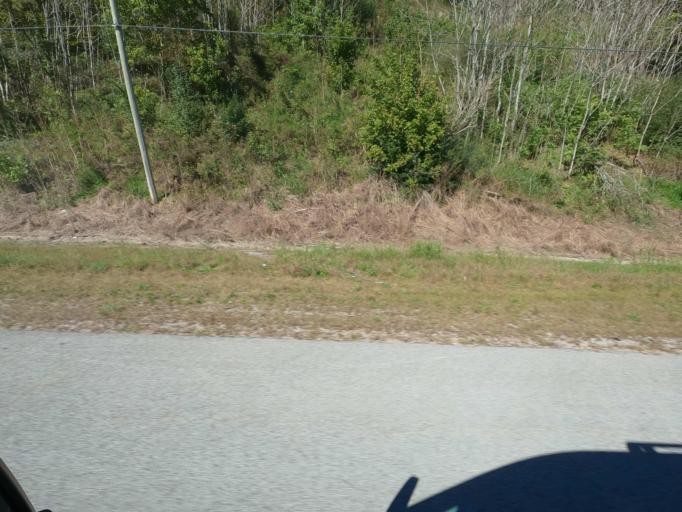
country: US
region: Tennessee
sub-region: Maury County
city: Mount Pleasant
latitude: 35.4829
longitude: -87.2545
